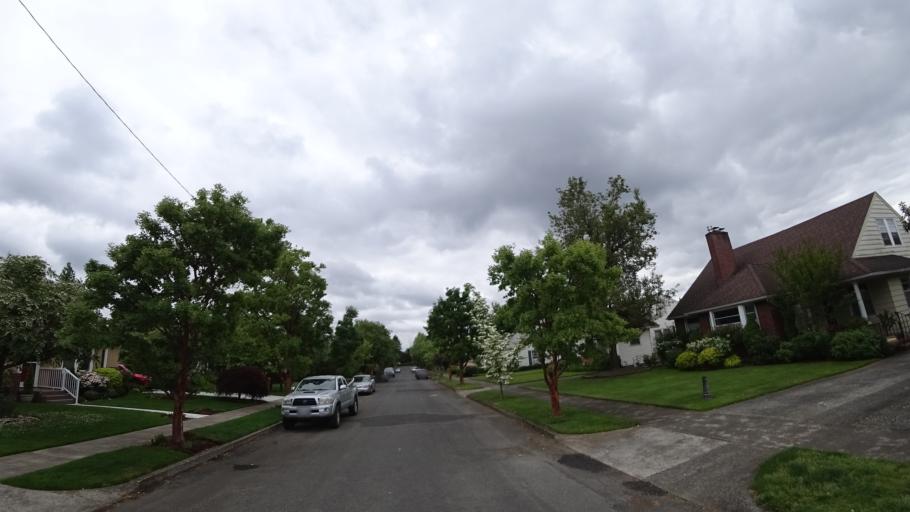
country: US
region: Oregon
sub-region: Multnomah County
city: Portland
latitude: 45.5218
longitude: -122.6140
